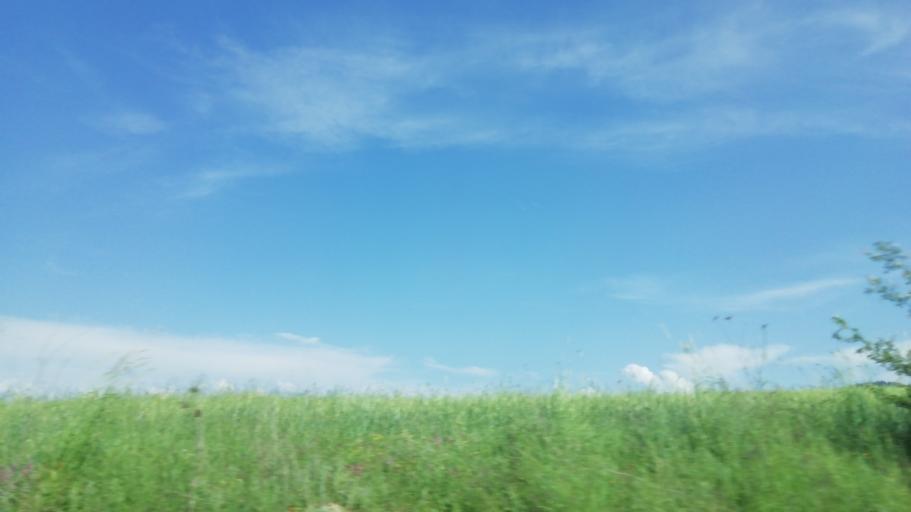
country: TR
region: Karabuk
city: Karabuk
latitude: 41.0953
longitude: 32.5918
